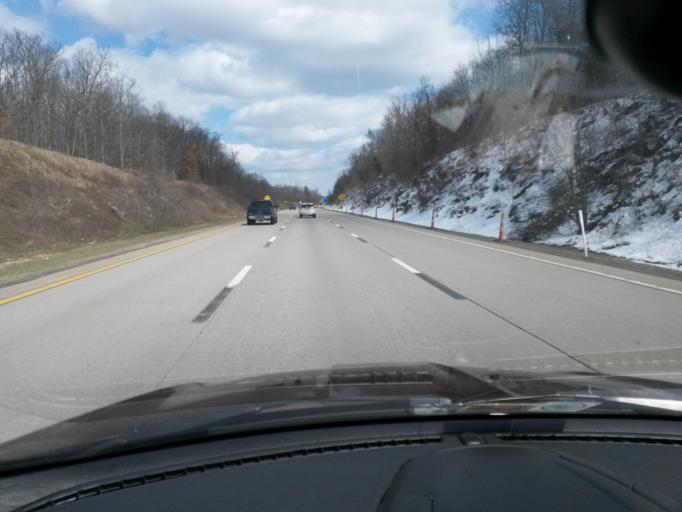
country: US
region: West Virginia
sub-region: Raleigh County
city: Daniels
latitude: 37.7731
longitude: -81.0999
